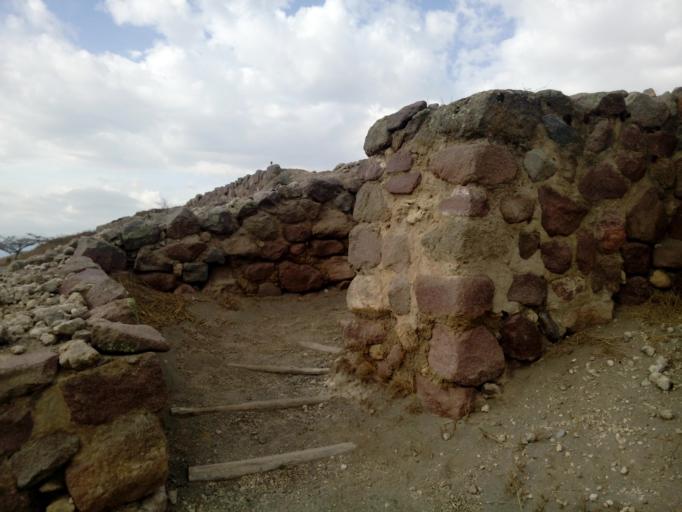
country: EC
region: Pichincha
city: Quito
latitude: 0.0074
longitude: -78.4311
